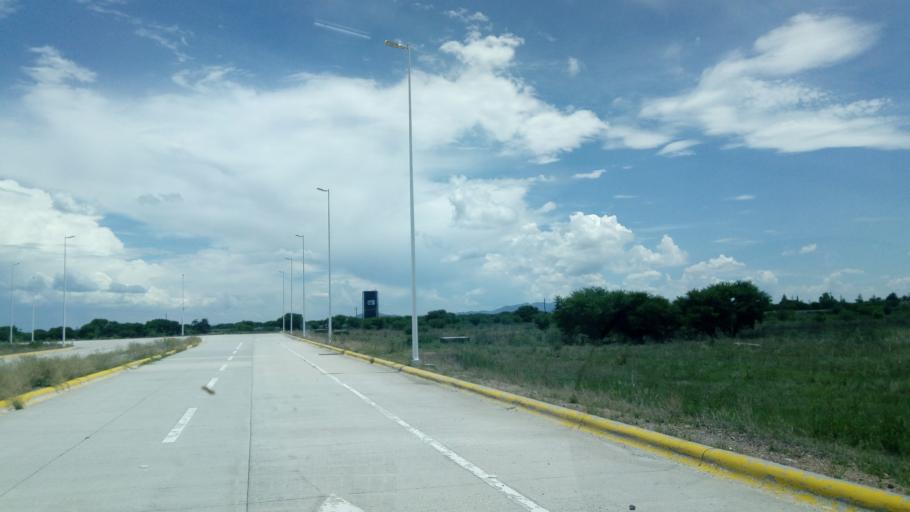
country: MX
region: Durango
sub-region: Durango
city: Jose Refugio Salcido
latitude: 24.1597
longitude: -104.5141
